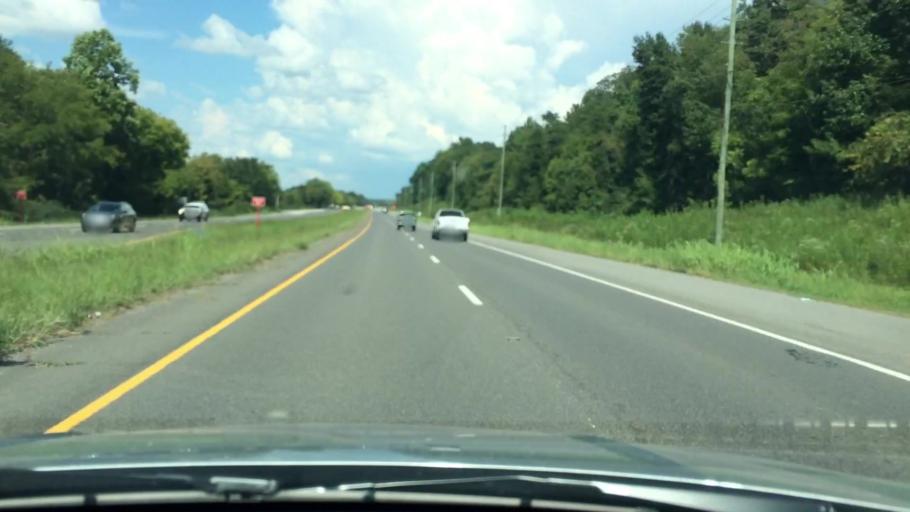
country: US
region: Tennessee
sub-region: Monroe County
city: Vonore
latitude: 35.6077
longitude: -84.2086
